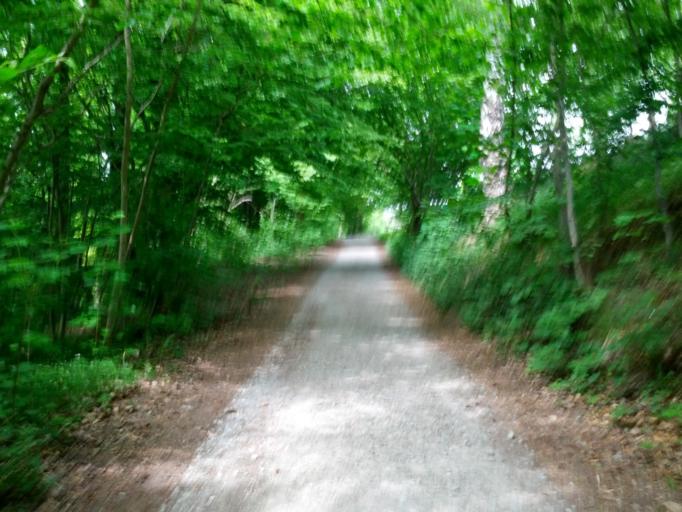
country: DE
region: Thuringia
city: Seebach
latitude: 50.9446
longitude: 10.4444
